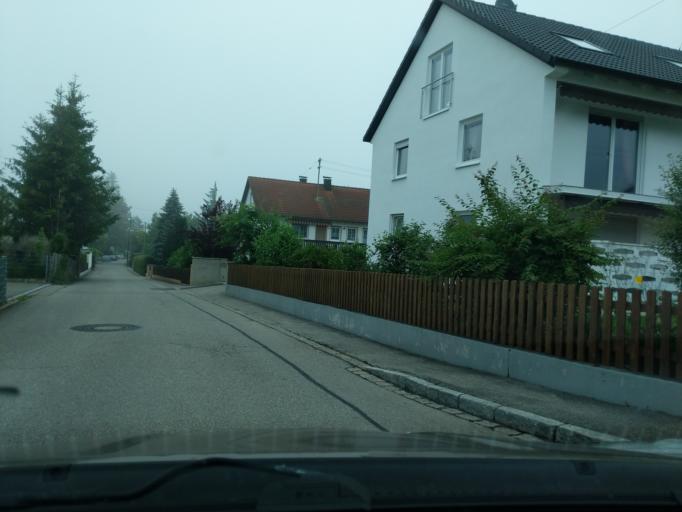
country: DE
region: Bavaria
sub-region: Swabia
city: Gessertshausen
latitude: 48.3298
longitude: 10.7379
